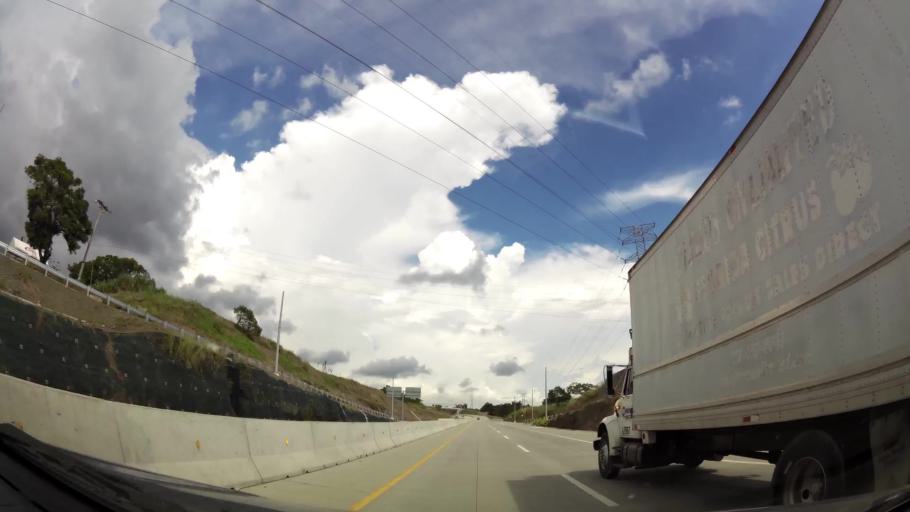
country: PA
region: Panama
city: Tocumen
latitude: 9.0912
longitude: -79.4305
